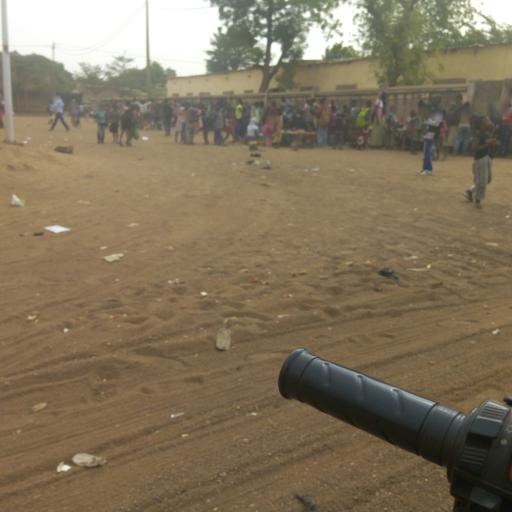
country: ML
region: Bamako
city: Bamako
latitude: 12.6667
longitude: -7.9454
